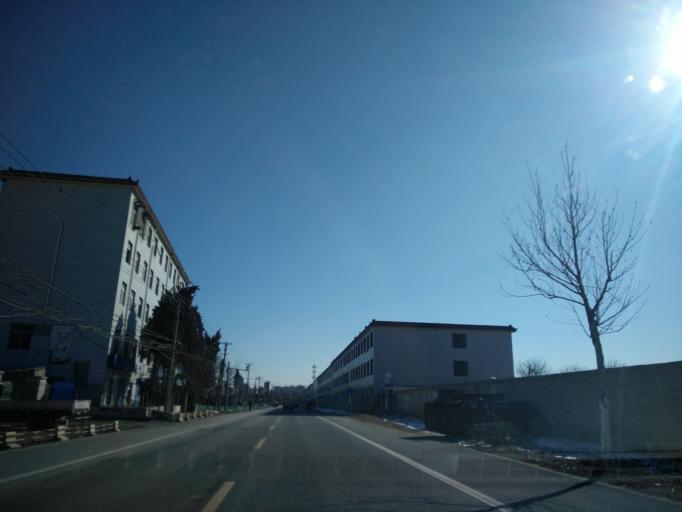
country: CN
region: Beijing
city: Yinghai
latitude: 39.7534
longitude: 116.4612
